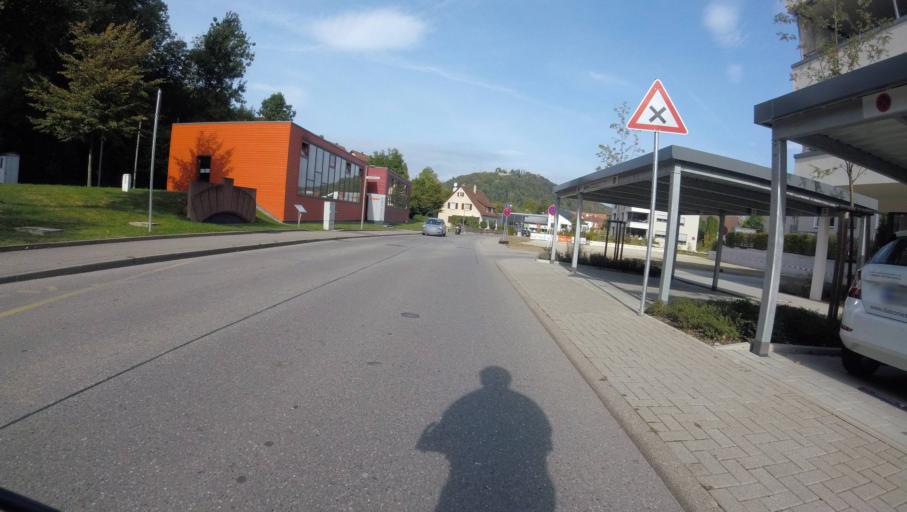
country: DE
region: Baden-Wuerttemberg
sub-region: Karlsruhe Region
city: Nagold
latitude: 48.5460
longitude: 8.7260
